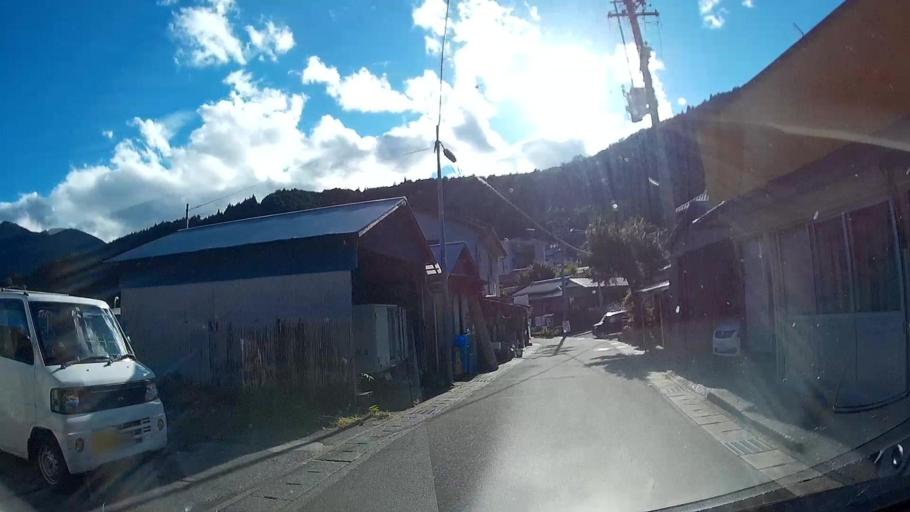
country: JP
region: Shizuoka
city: Shizuoka-shi
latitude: 35.2214
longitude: 138.2411
